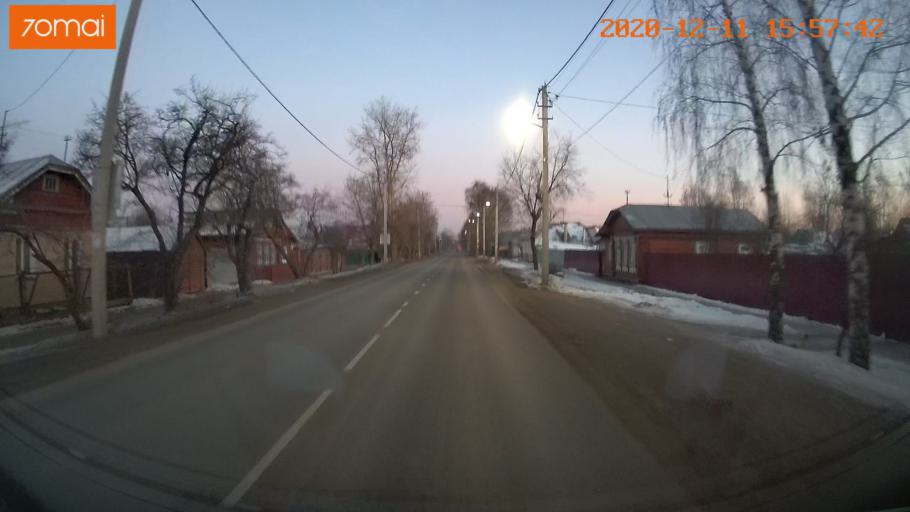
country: RU
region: Ivanovo
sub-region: Gorod Ivanovo
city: Ivanovo
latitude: 56.9814
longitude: 40.9434
